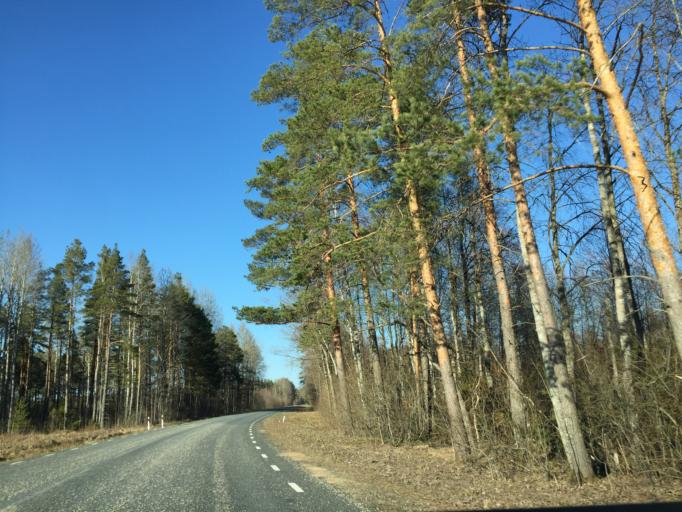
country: RU
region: Pskov
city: Gdov
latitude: 59.0137
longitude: 27.6824
